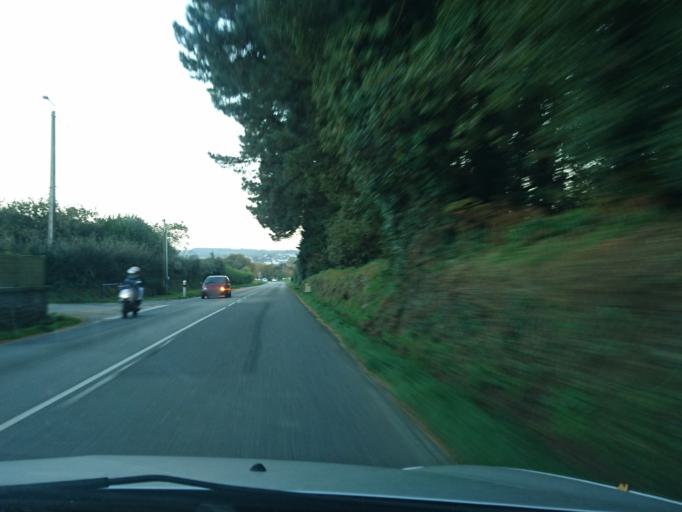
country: FR
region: Brittany
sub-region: Departement du Finistere
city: Saint-Renan
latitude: 48.4469
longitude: -4.6227
